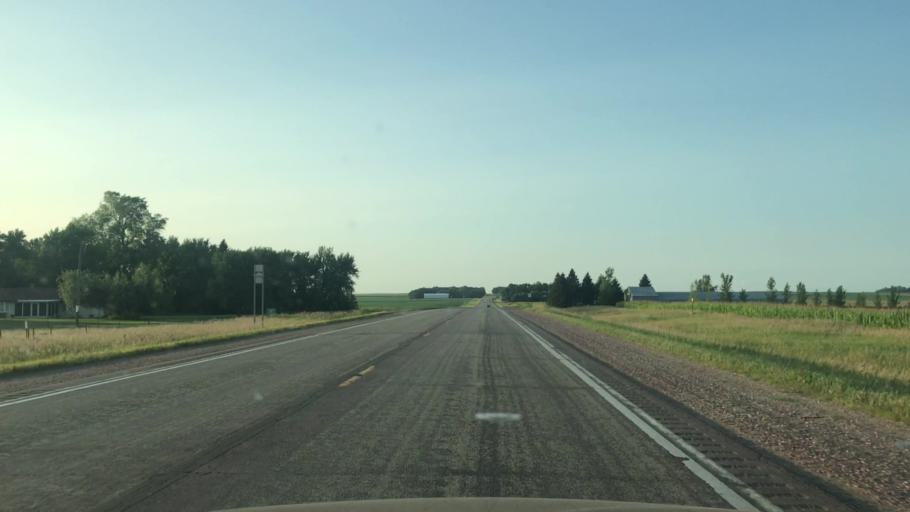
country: US
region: Minnesota
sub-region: Cottonwood County
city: Windom
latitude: 43.9087
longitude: -95.1203
